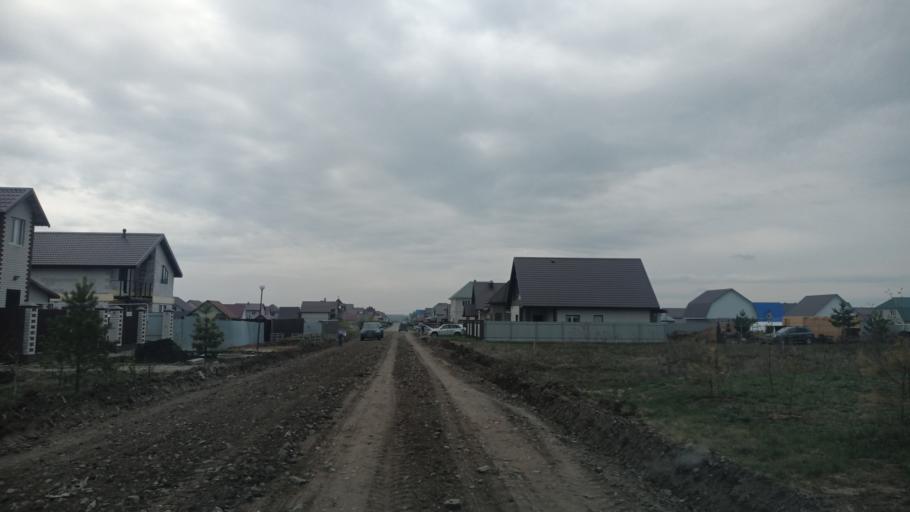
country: RU
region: Altai Krai
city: Yuzhnyy
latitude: 53.2265
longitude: 83.6910
